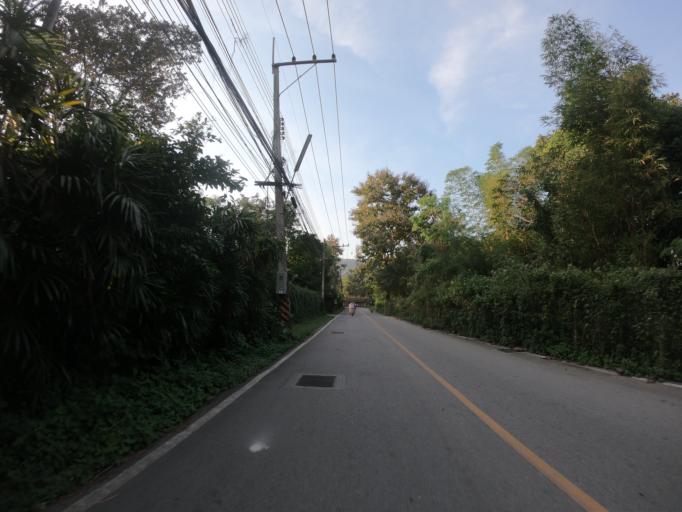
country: TH
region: Chiang Mai
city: Chiang Mai
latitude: 18.8169
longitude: 98.9552
